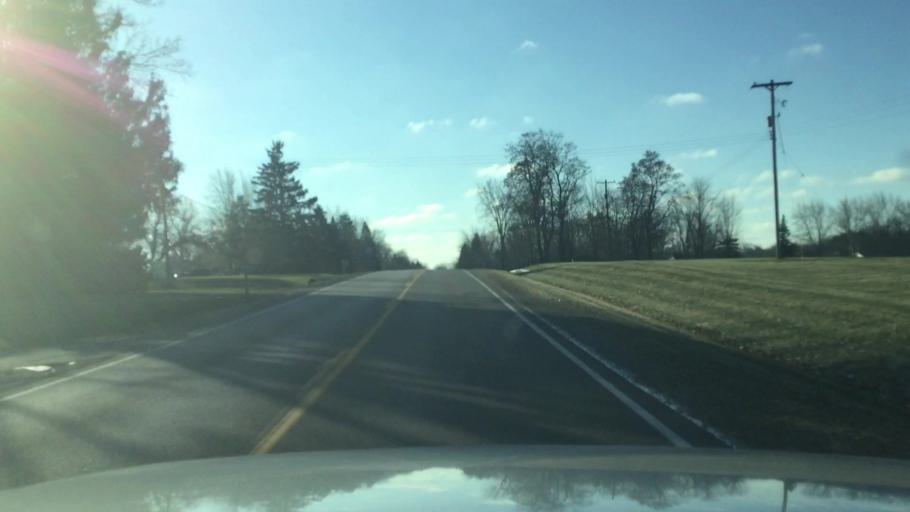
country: US
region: Michigan
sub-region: Genesee County
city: Grand Blanc
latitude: 42.9318
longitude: -83.6620
